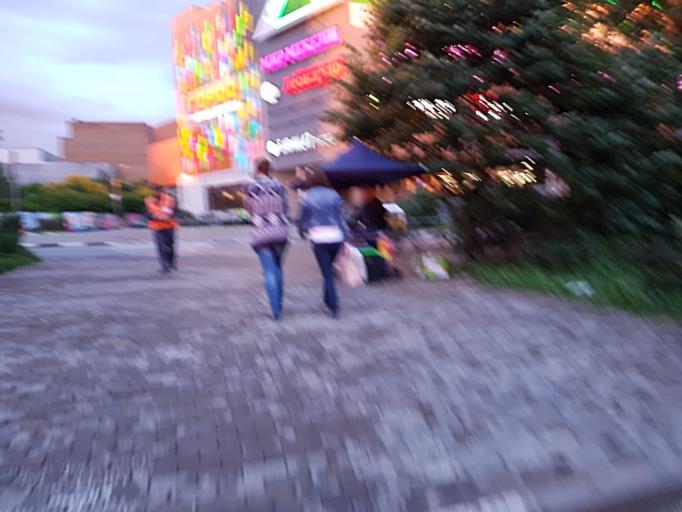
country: RU
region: Moscow
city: Tekstil'shchiki
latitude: 55.7306
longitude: 37.7333
